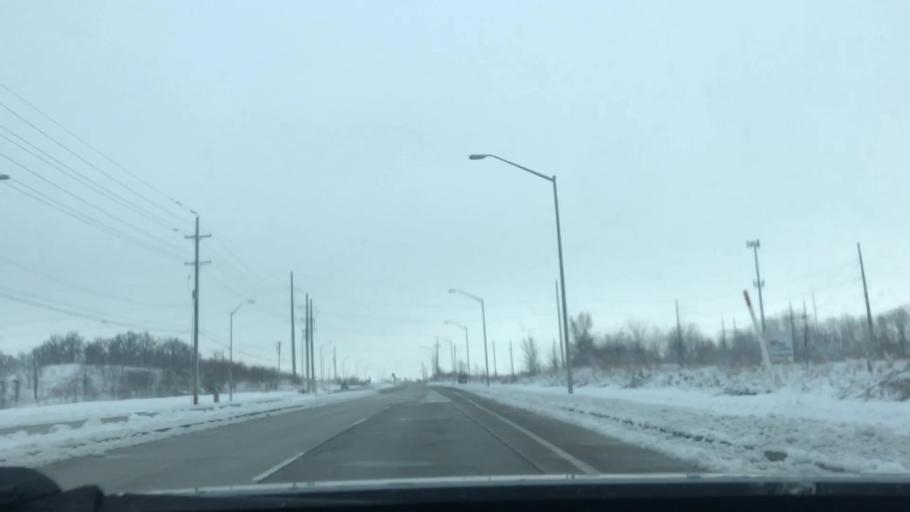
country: US
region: Missouri
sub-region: Platte County
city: Weatherby Lake
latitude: 39.2580
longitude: -94.6680
